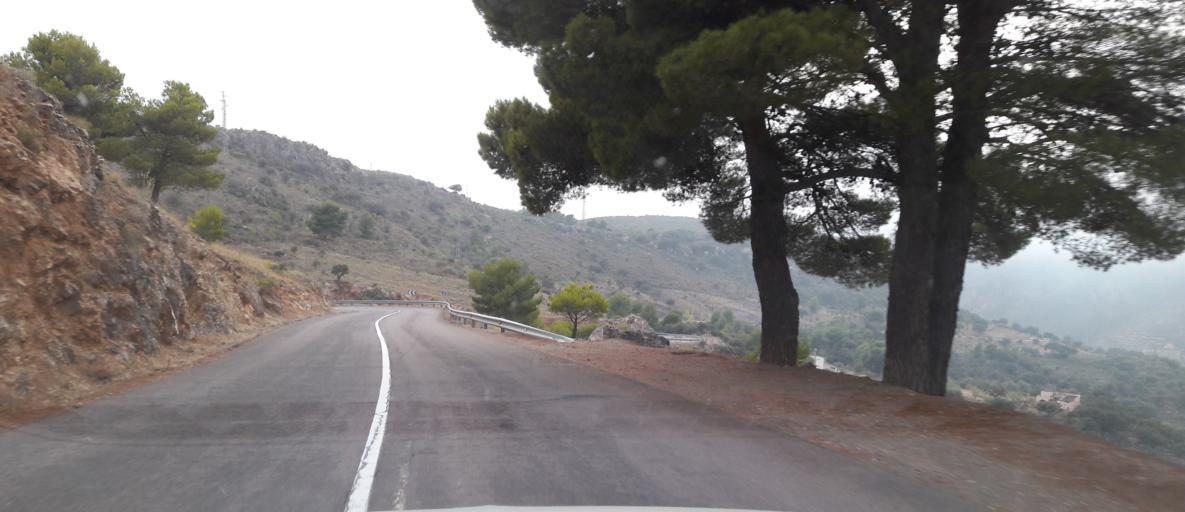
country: ES
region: Andalusia
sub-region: Provincia de Almeria
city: Enix
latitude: 36.8954
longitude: -2.6110
